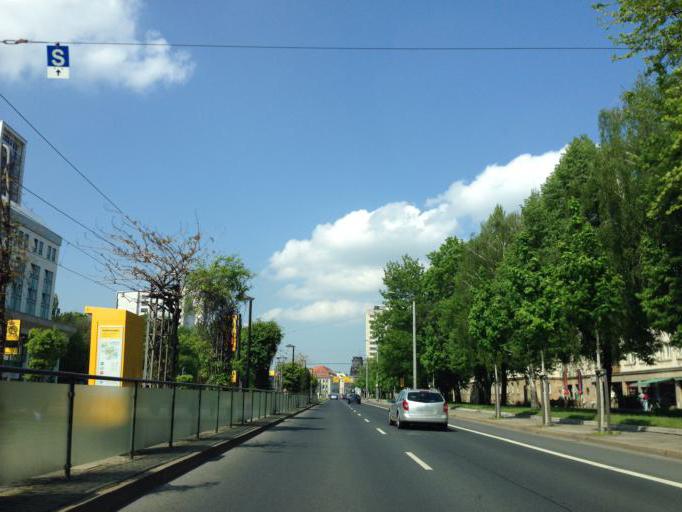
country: DE
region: Saxony
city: Dresden
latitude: 51.0475
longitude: 13.7506
